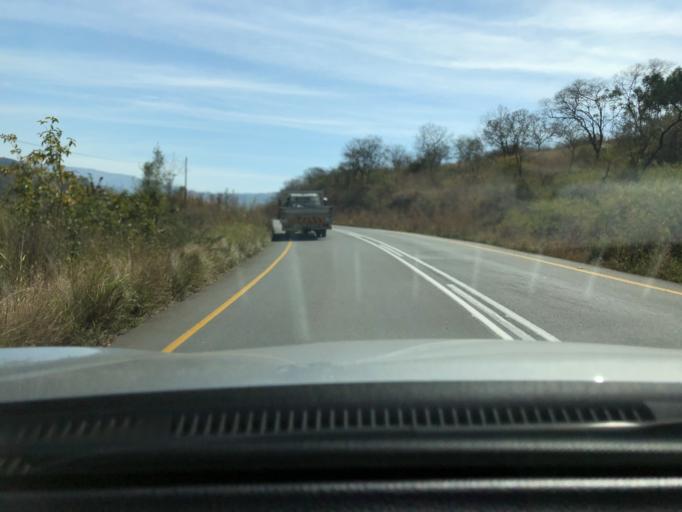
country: ZA
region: KwaZulu-Natal
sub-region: uMgungundlovu District Municipality
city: Richmond
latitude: -29.9579
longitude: 30.2555
